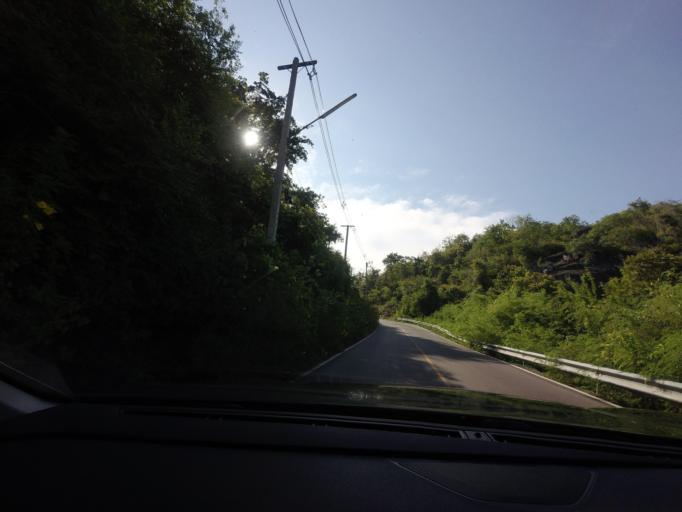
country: TH
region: Prachuap Khiri Khan
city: Pran Buri
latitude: 12.4102
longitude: 99.9769
